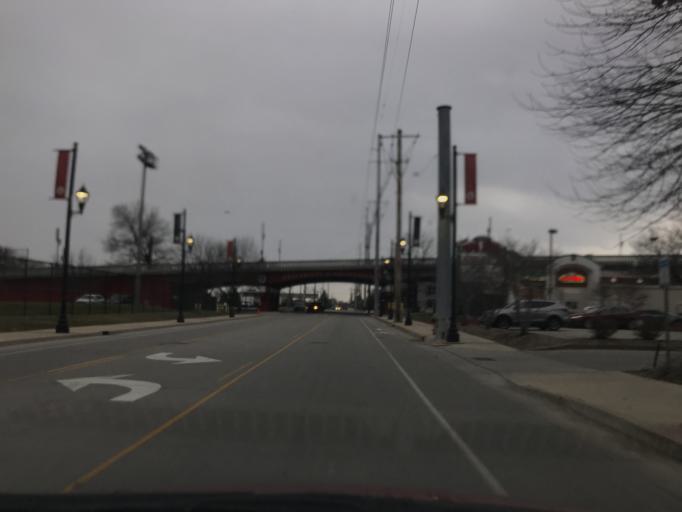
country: US
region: Kentucky
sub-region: Jefferson County
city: Audubon Park
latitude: 38.2140
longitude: -85.7553
